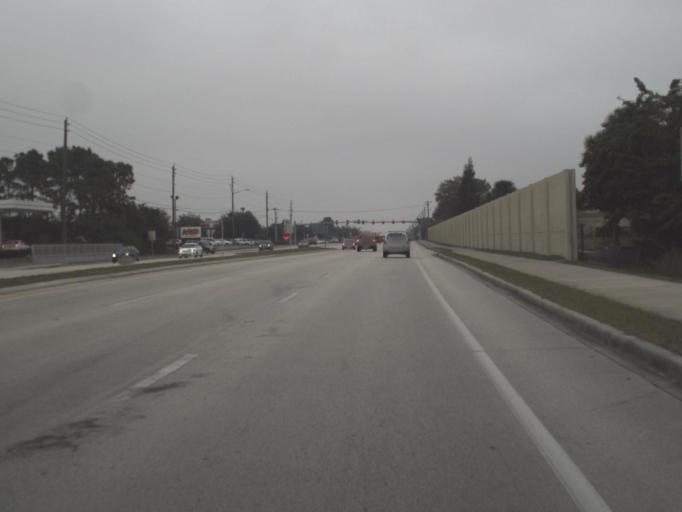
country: US
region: Florida
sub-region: Brevard County
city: West Melbourne
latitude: 28.0352
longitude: -80.6414
